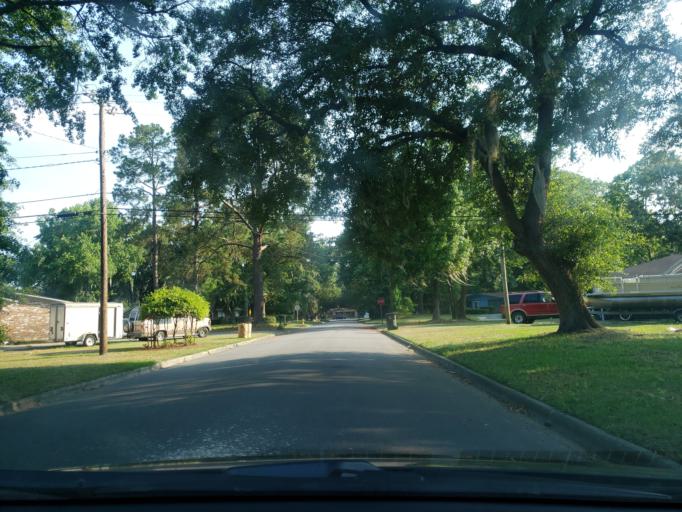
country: US
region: Georgia
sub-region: Chatham County
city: Montgomery
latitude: 31.9873
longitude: -81.1408
